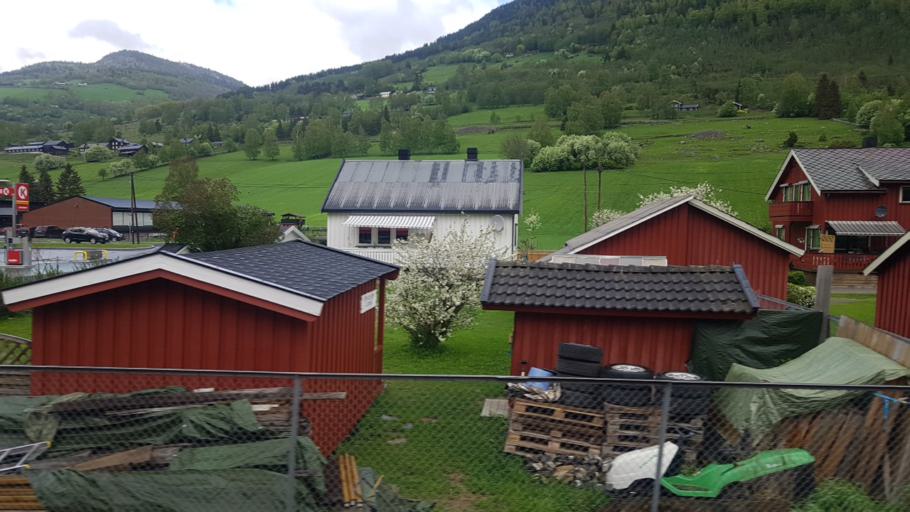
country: NO
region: Oppland
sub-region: Nord-Fron
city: Vinstra
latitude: 61.6640
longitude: 9.6688
